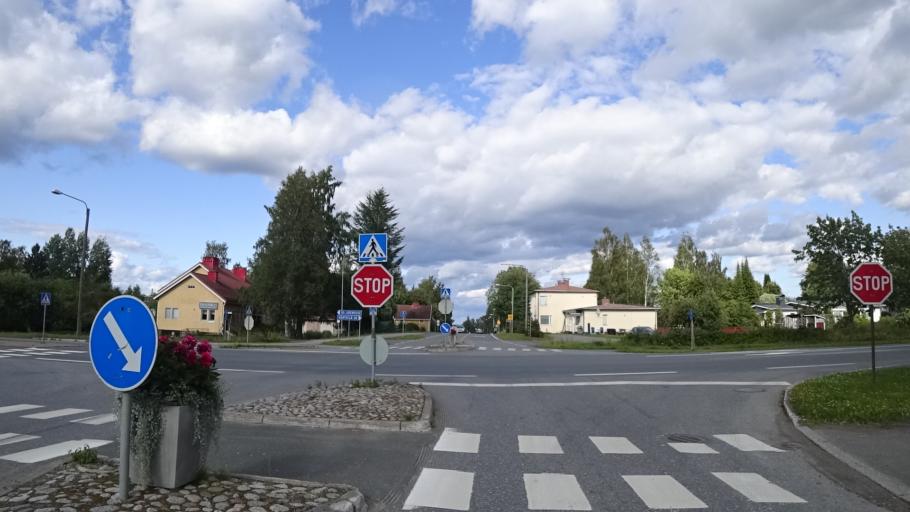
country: FI
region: North Karelia
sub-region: Keski-Karjala
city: Tohmajaervi
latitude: 62.2261
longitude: 30.3322
